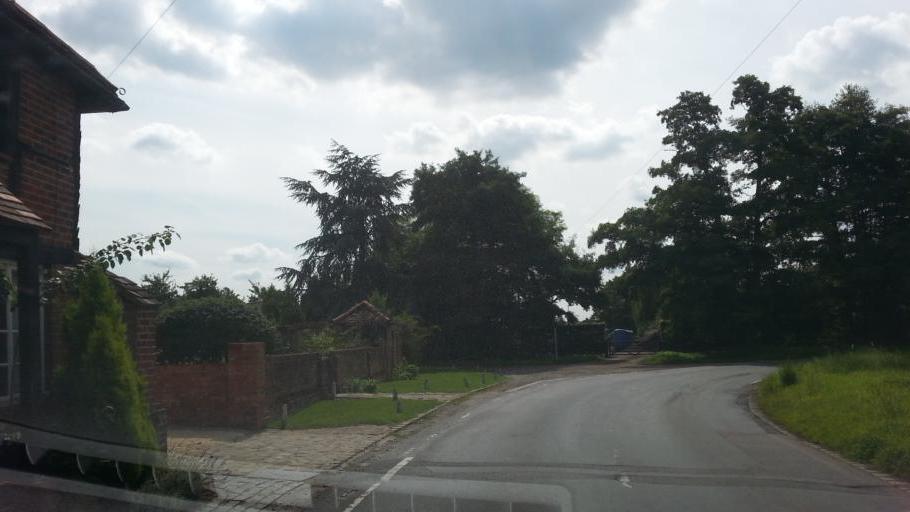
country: GB
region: England
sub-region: Surrey
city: Woking
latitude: 51.3477
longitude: -0.5700
